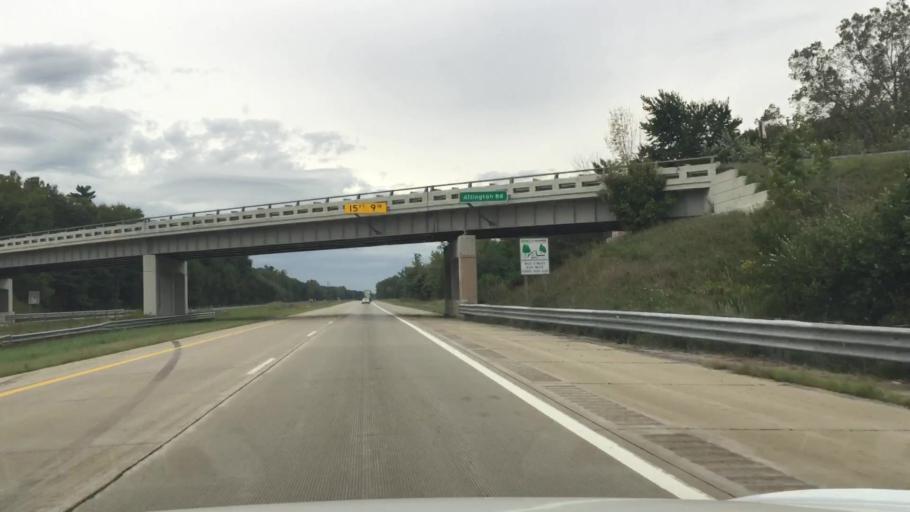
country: US
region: Michigan
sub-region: Saint Clair County
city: Saint Clair
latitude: 42.8358
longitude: -82.5954
